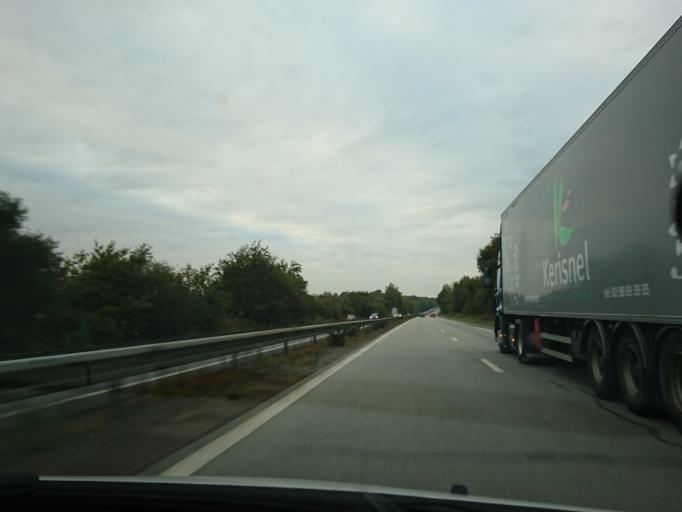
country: FR
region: Brittany
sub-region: Departement du Morbihan
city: Nostang
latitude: 47.7708
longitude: -3.1750
